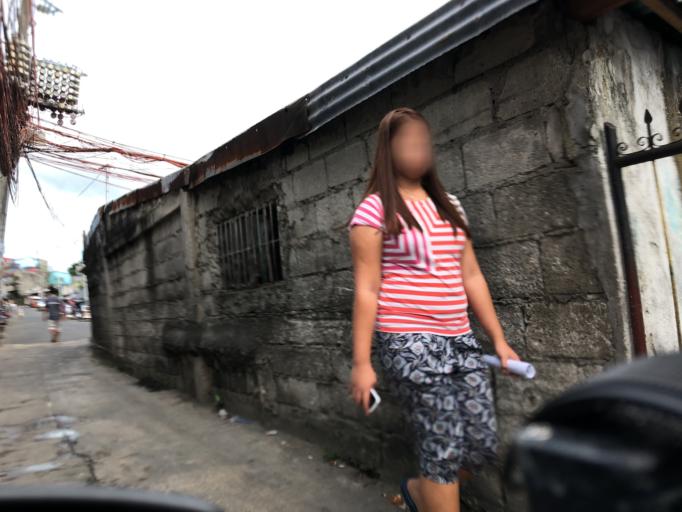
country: PH
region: Central Luzon
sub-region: Province of Bulacan
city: San Jose del Monte
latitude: 14.7672
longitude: 121.0527
